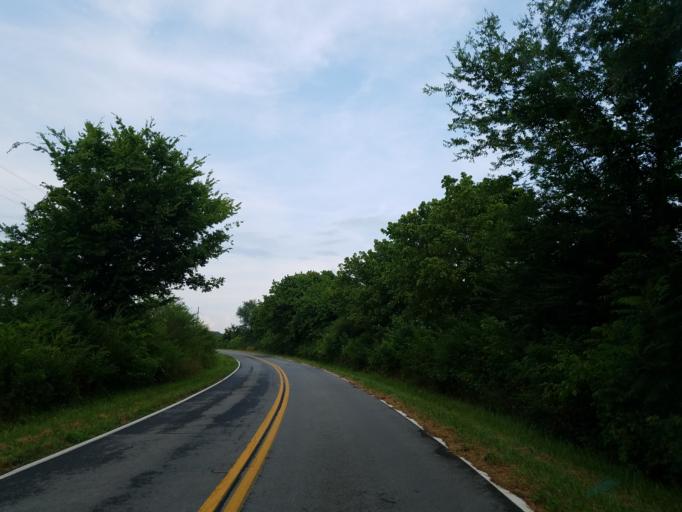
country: US
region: Georgia
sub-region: Pickens County
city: Jasper
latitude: 34.4502
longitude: -84.5621
